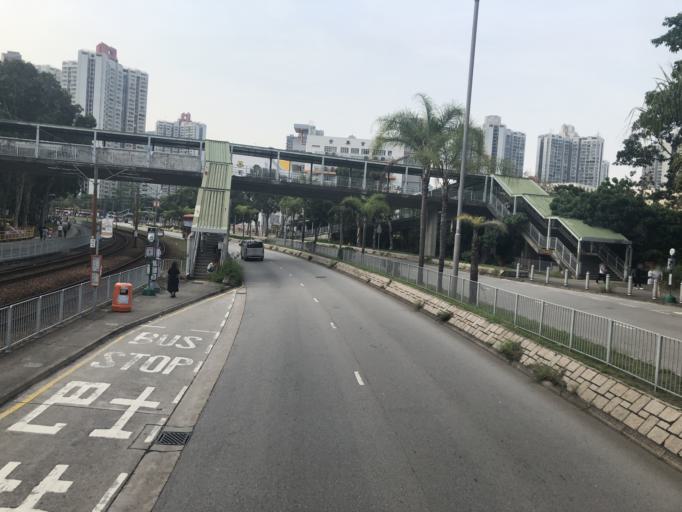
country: HK
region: Tuen Mun
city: Tuen Mun
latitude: 22.4018
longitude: 113.9678
